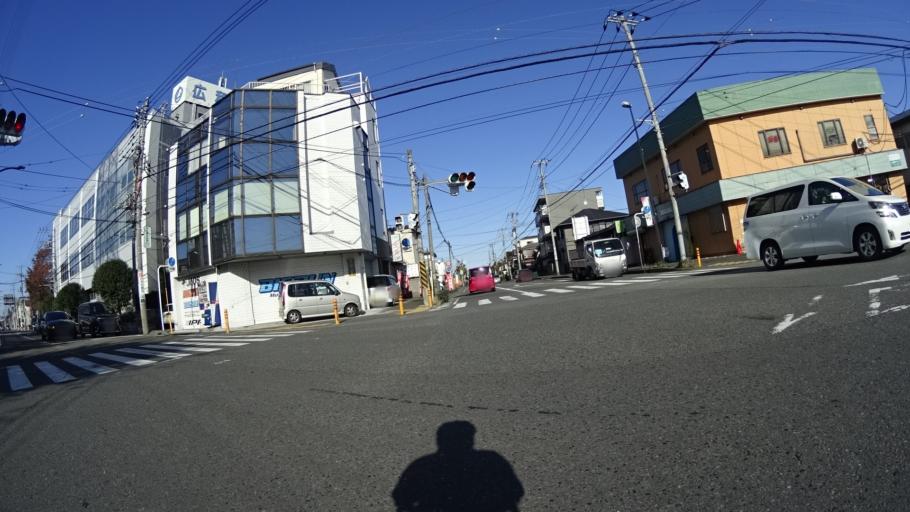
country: JP
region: Tokyo
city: Hachioji
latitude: 35.5824
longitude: 139.3618
